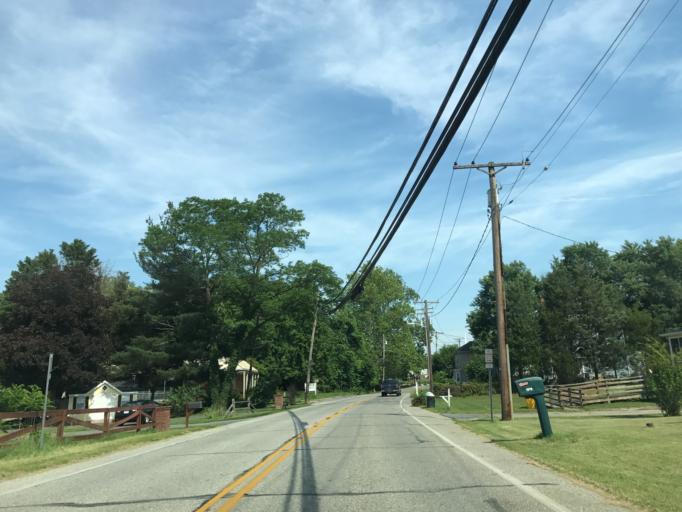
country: US
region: Maryland
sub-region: Anne Arundel County
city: Odenton
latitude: 39.0858
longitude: -76.7028
